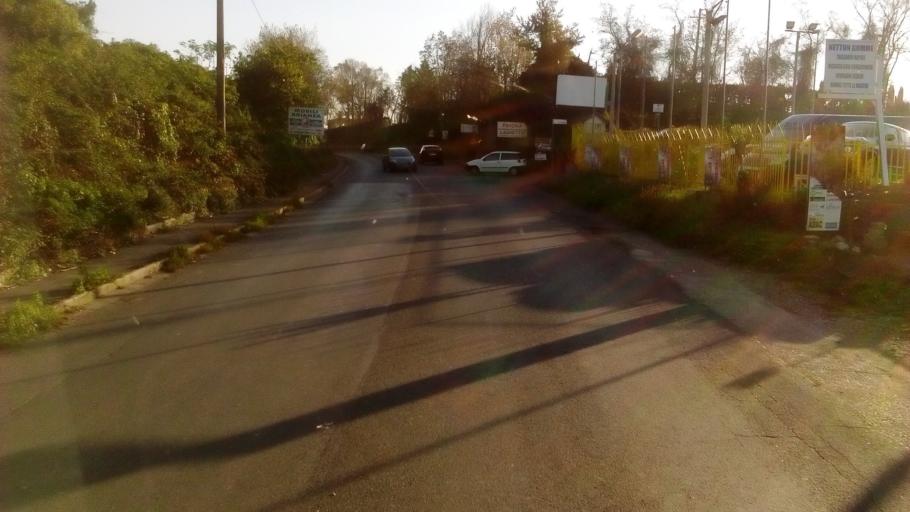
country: IT
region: Latium
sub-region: Citta metropolitana di Roma Capitale
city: Pavona
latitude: 41.7381
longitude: 12.6159
